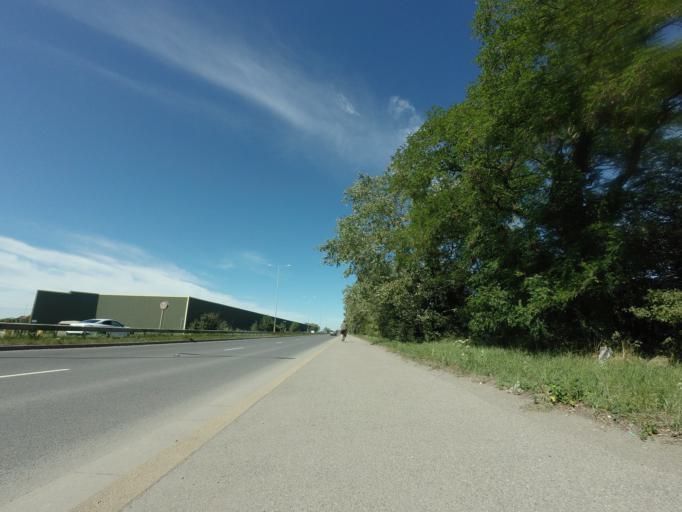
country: GB
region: England
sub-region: Kent
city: Sandwich
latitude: 51.3042
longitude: 1.3475
